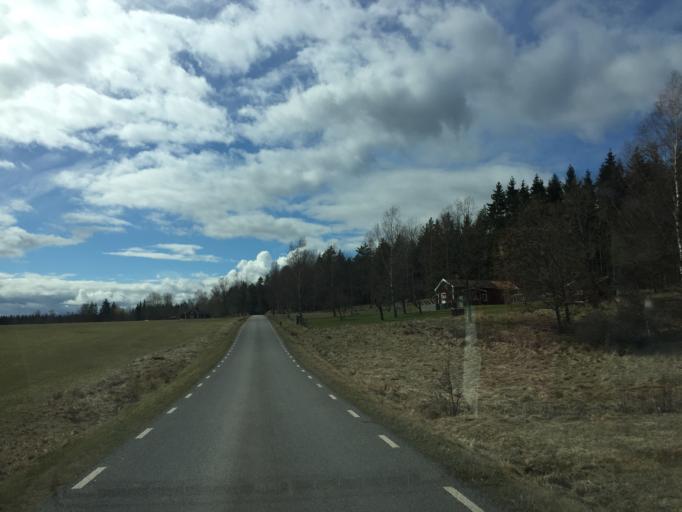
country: SE
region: Soedermanland
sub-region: Nykopings Kommun
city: Stigtomta
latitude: 58.9831
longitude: 16.9234
